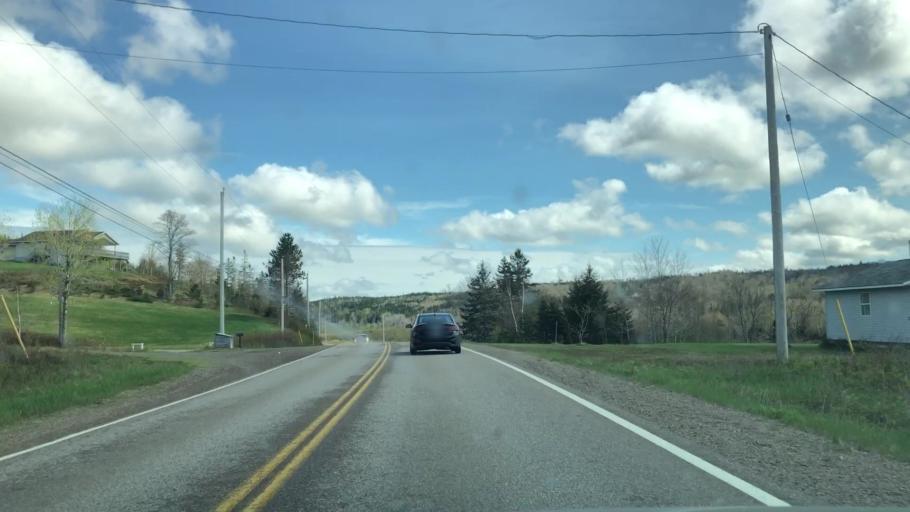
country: CA
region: Nova Scotia
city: Antigonish
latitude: 45.1981
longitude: -62.0023
